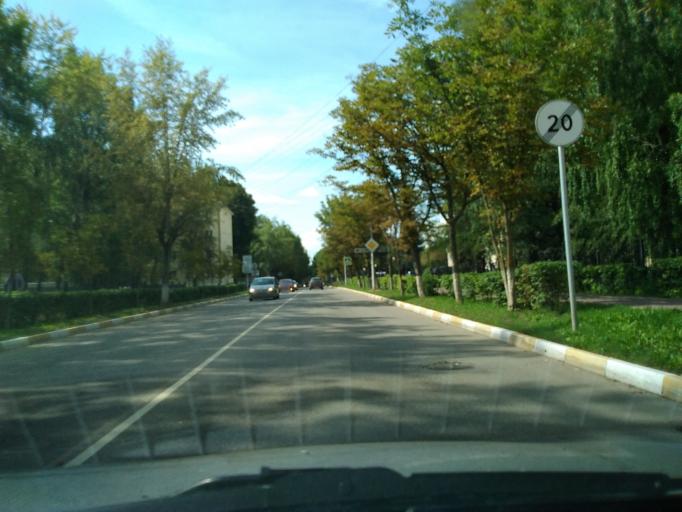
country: RU
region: Moskovskaya
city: Voskresensk
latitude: 55.3250
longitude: 38.6673
